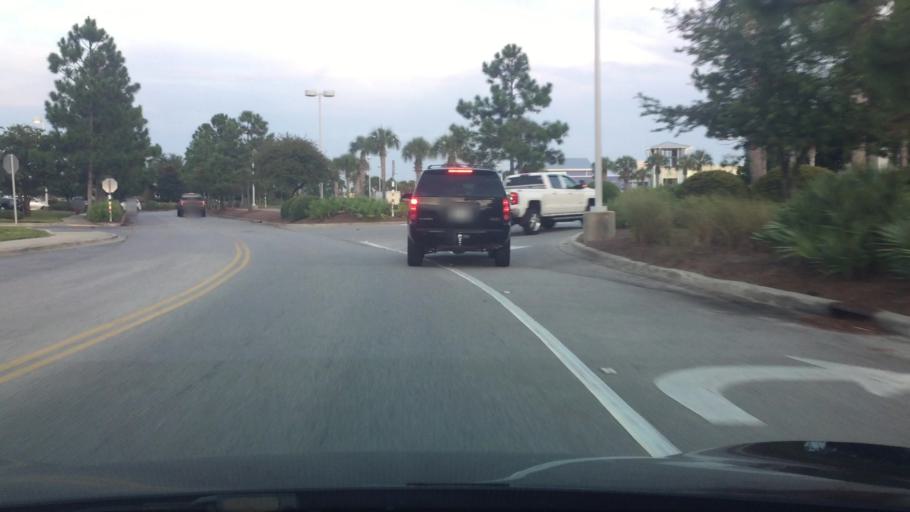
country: US
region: Florida
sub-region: Bay County
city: Laguna Beach
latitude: 30.2227
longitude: -85.8719
